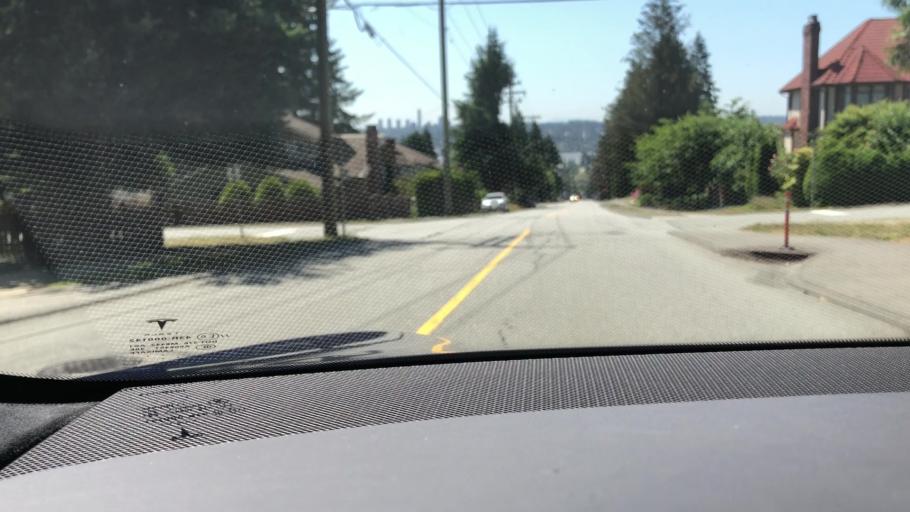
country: CA
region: British Columbia
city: Port Moody
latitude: 49.2475
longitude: -122.8652
